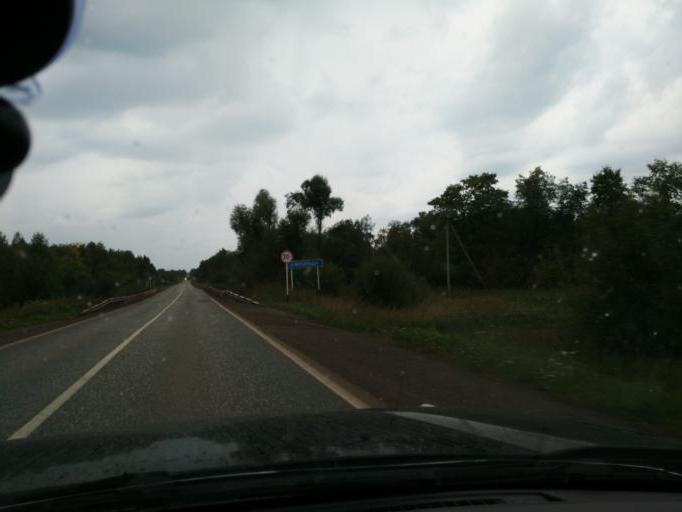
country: RU
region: Perm
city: Barda
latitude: 56.8523
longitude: 55.9417
